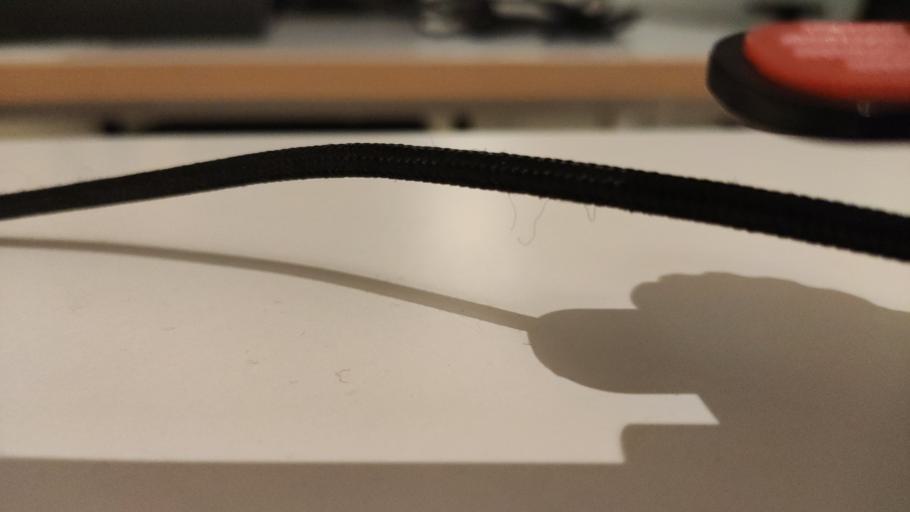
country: RU
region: Moskovskaya
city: Rybnoye
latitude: 56.4021
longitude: 37.6410
